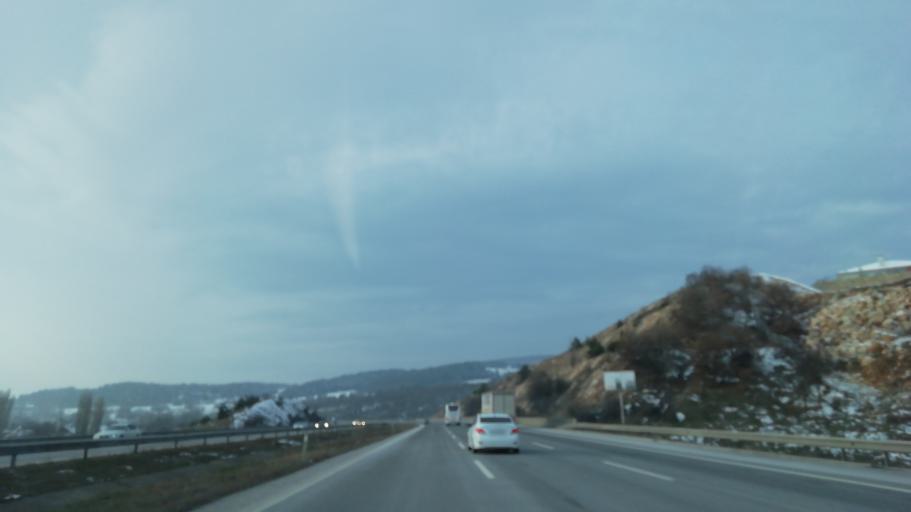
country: TR
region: Bolu
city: Bolu
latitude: 40.7397
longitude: 31.5481
